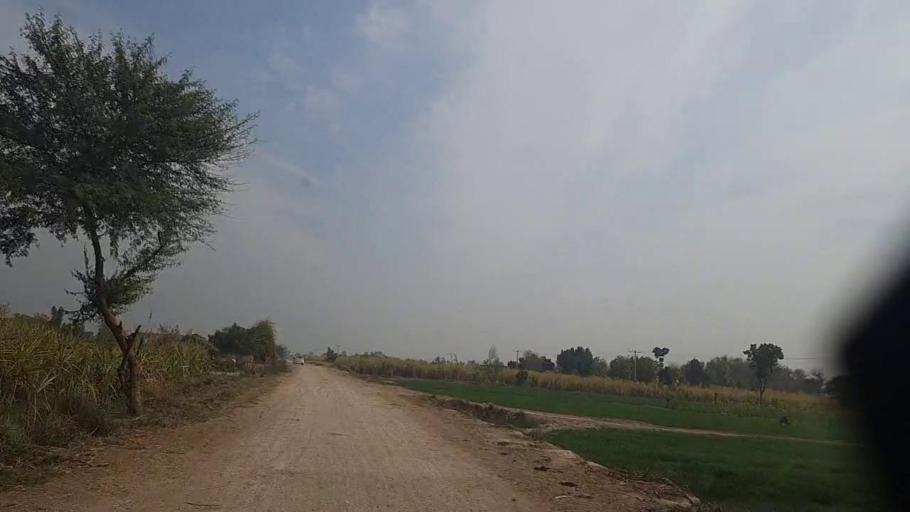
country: PK
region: Sindh
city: Daur
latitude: 26.3315
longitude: 68.1941
